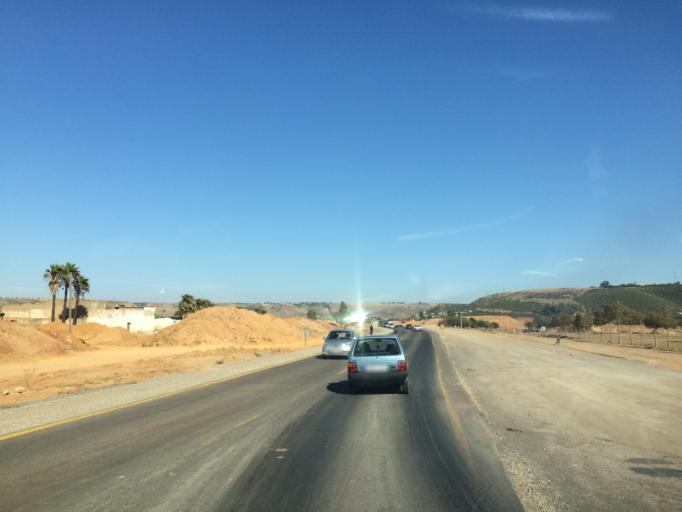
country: MA
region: Rabat-Sale-Zemmour-Zaer
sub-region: Rabat
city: Rabat
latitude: 33.9899
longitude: -6.7953
